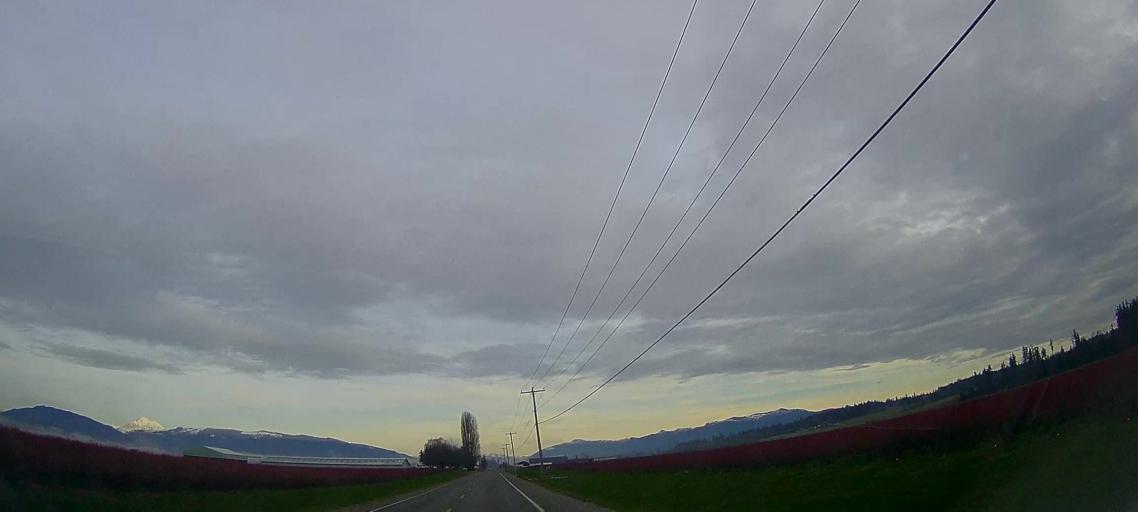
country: US
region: Washington
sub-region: Skagit County
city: Anacortes
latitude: 48.5195
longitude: -122.4695
